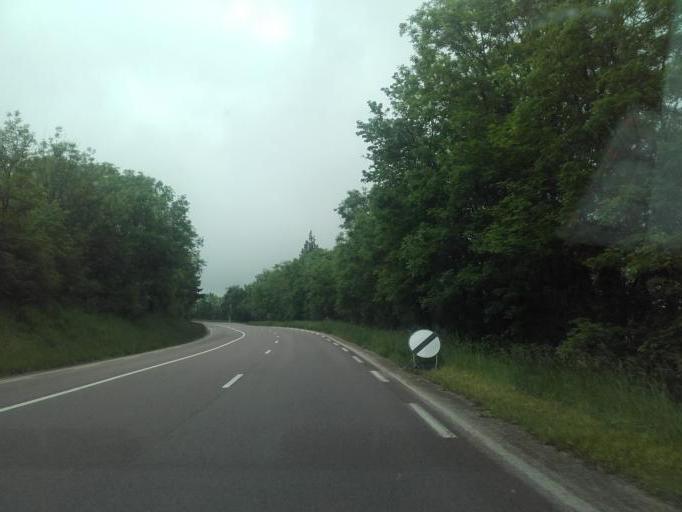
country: FR
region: Bourgogne
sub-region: Departement de la Cote-d'Or
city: Nolay
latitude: 46.9660
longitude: 4.6778
